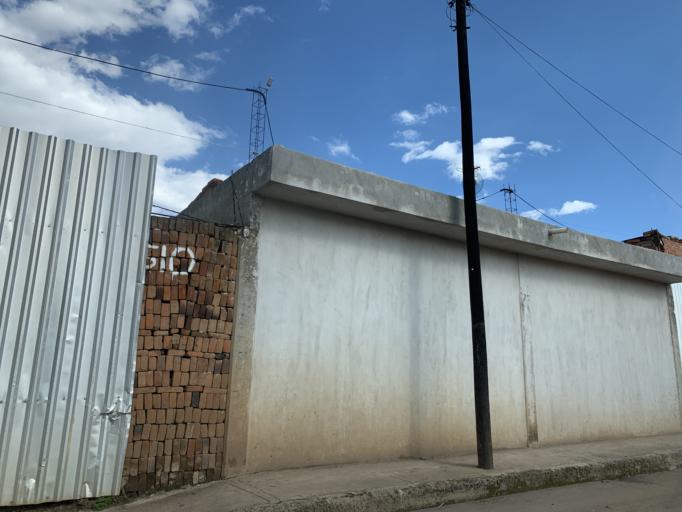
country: MX
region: Puebla
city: Cholula
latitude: 19.0733
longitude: -98.3089
